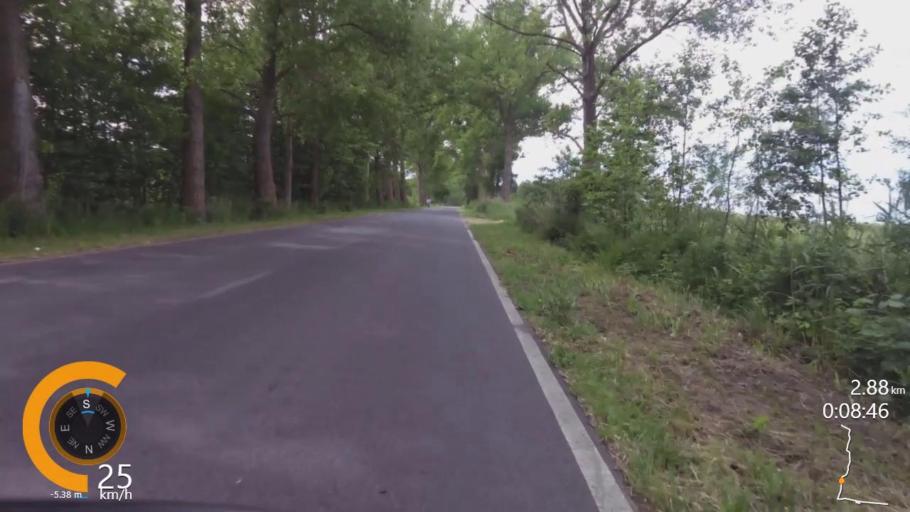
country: PL
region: West Pomeranian Voivodeship
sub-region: Powiat kamienski
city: Miedzyzdroje
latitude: 53.8886
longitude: 14.4343
